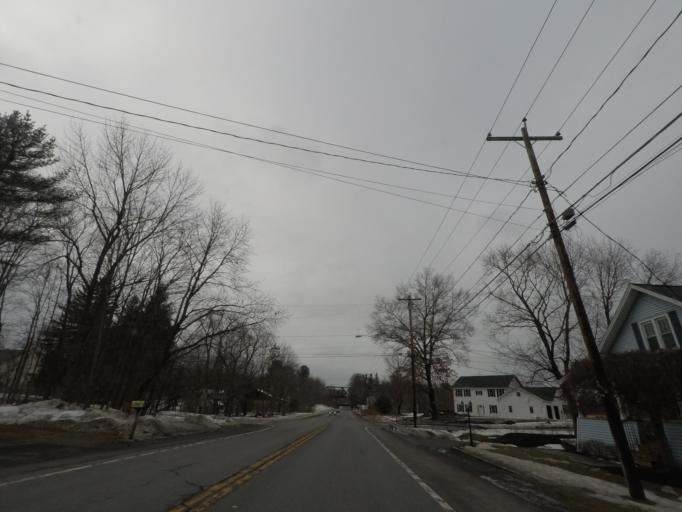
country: US
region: New York
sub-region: Schenectady County
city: Rotterdam
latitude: 42.7242
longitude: -73.9562
